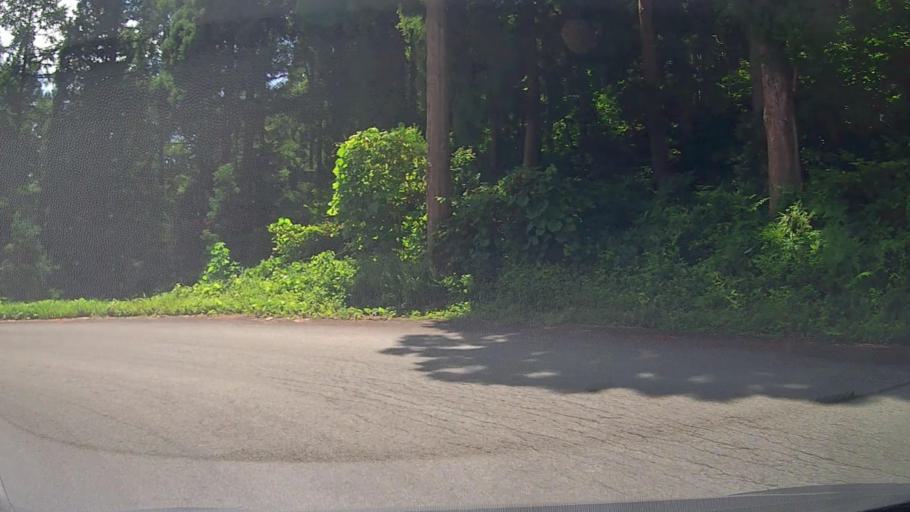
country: JP
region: Nagano
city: Iiyama
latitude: 36.9327
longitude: 138.4612
